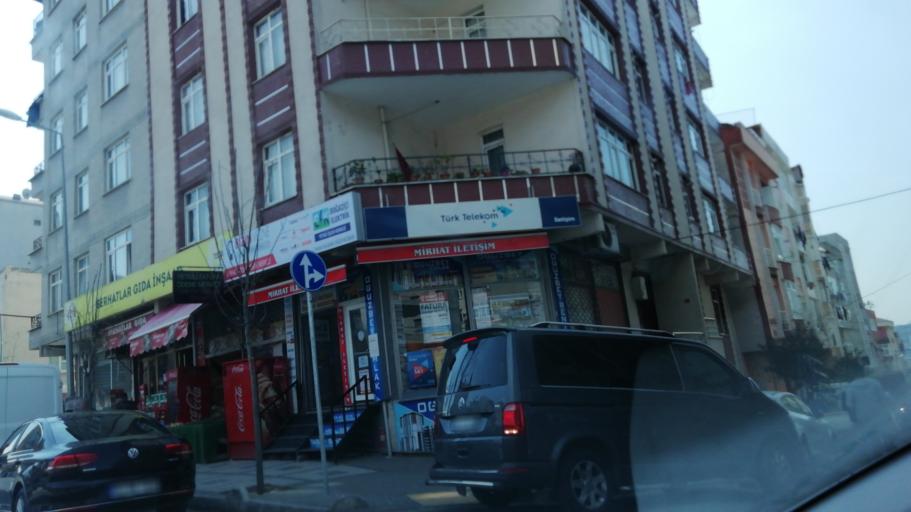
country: TR
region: Istanbul
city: Mahmutbey
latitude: 41.0361
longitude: 28.8199
